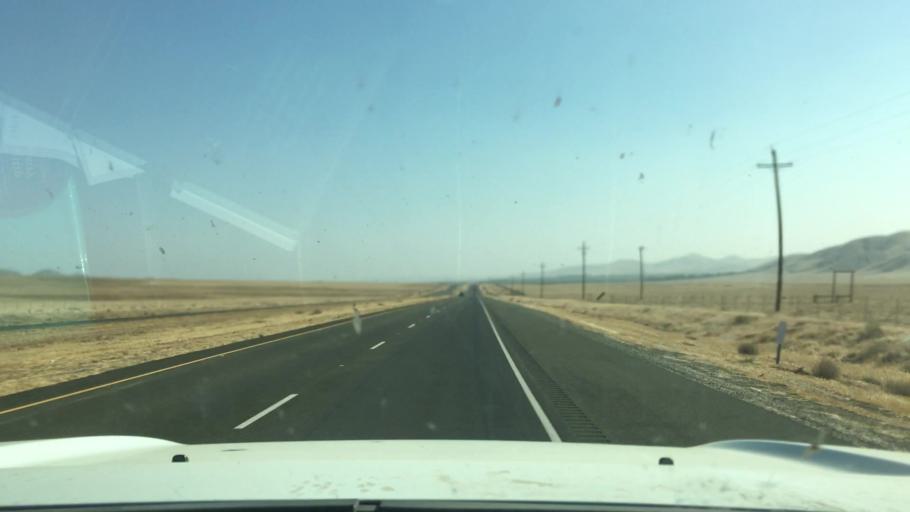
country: US
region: California
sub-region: San Luis Obispo County
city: Shandon
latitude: 35.7028
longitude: -120.1488
